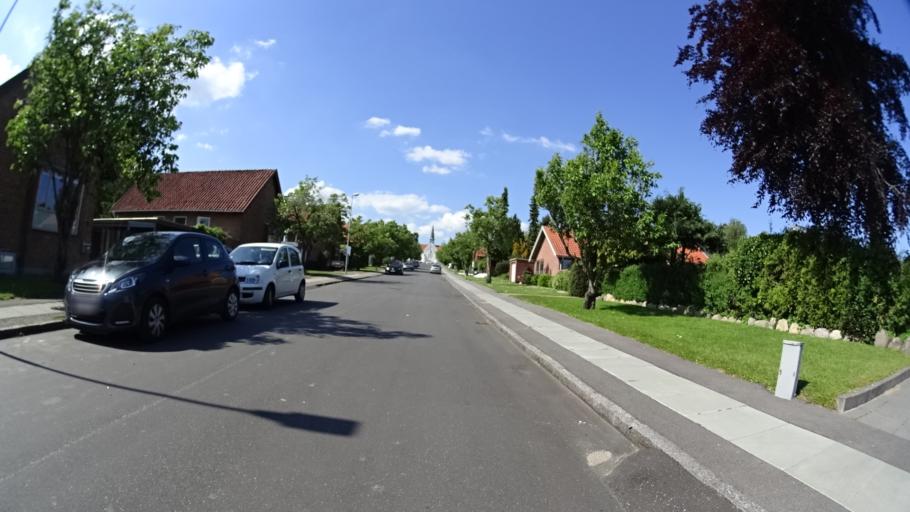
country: DK
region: Central Jutland
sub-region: Arhus Kommune
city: Stavtrup
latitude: 56.1527
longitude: 10.1593
